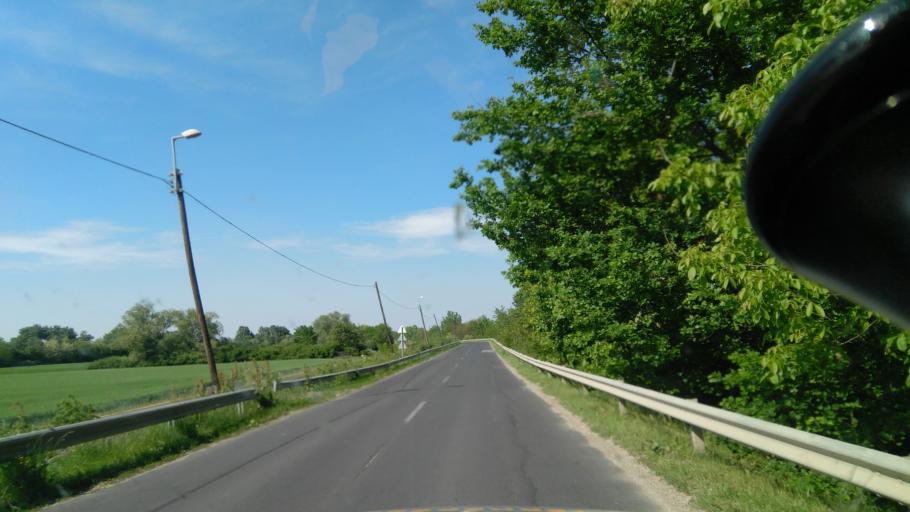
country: HU
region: Bekes
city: Gyula
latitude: 46.6662
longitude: 21.2984
